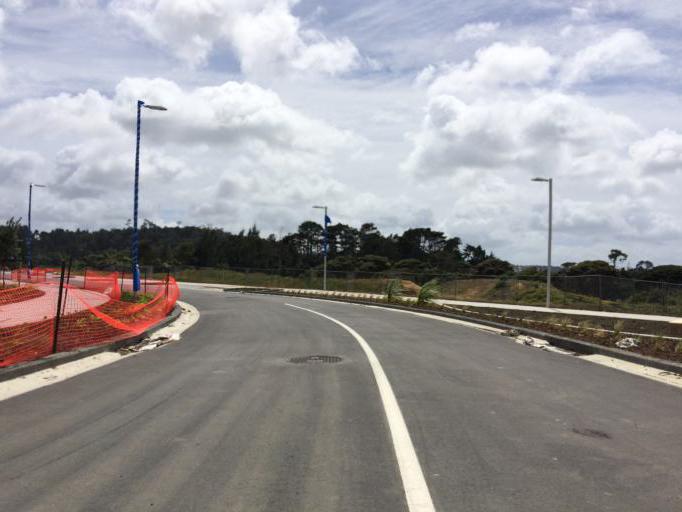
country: NZ
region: Auckland
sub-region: Auckland
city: North Shore
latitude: -36.7917
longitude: 174.6696
